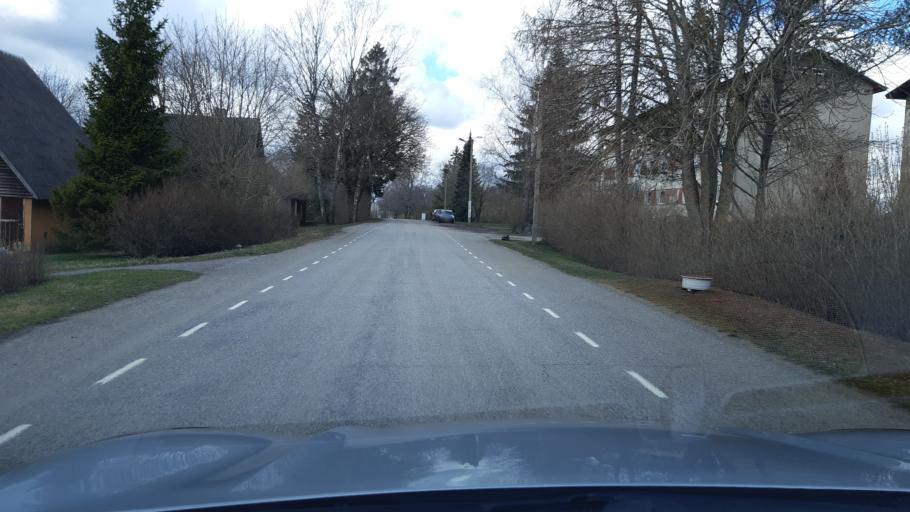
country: EE
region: Raplamaa
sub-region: Kehtna vald
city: Kehtna
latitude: 59.0411
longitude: 25.1244
